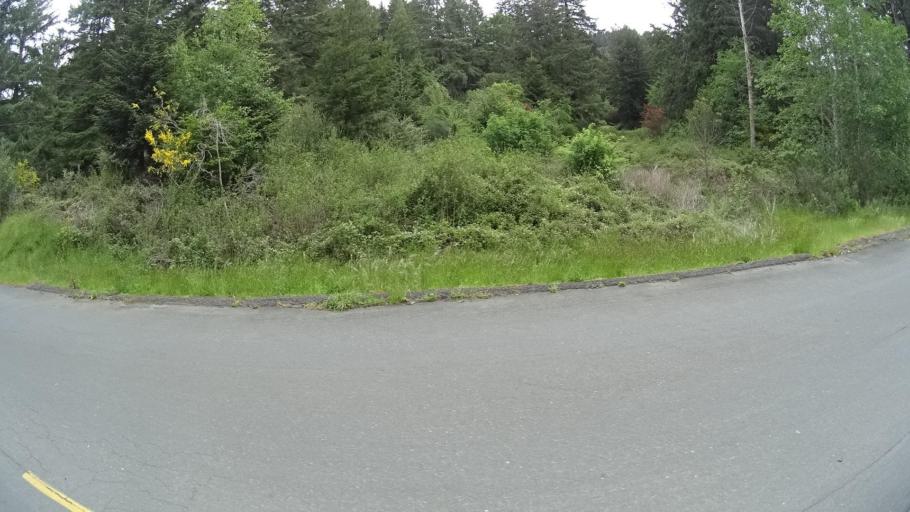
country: US
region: California
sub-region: Humboldt County
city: Bayside
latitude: 40.8536
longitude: -124.0569
